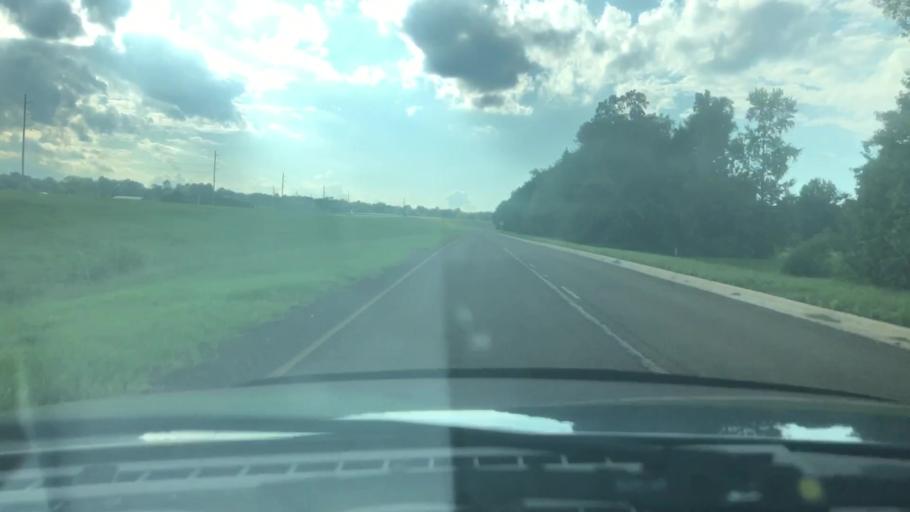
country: US
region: Texas
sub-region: Bowie County
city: Wake Village
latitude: 33.3865
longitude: -94.0824
